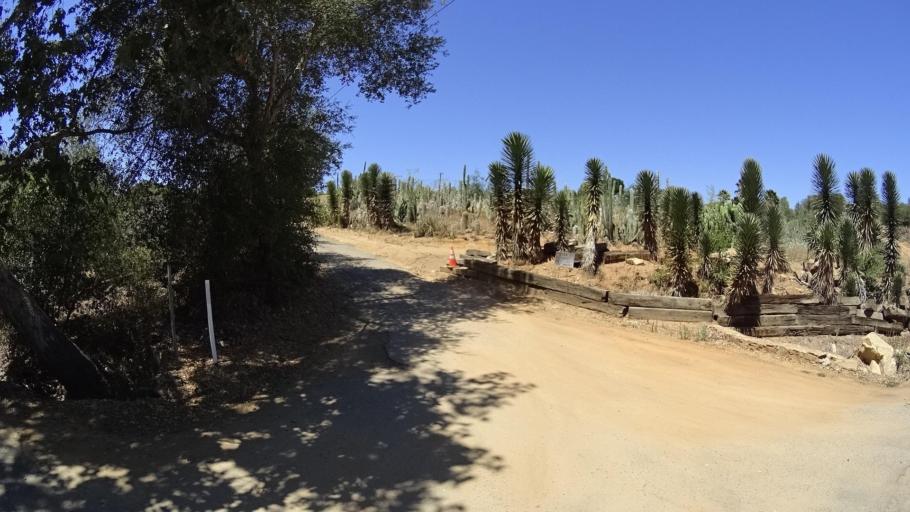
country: US
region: California
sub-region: San Diego County
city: Rainbow
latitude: 33.3804
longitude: -117.1424
